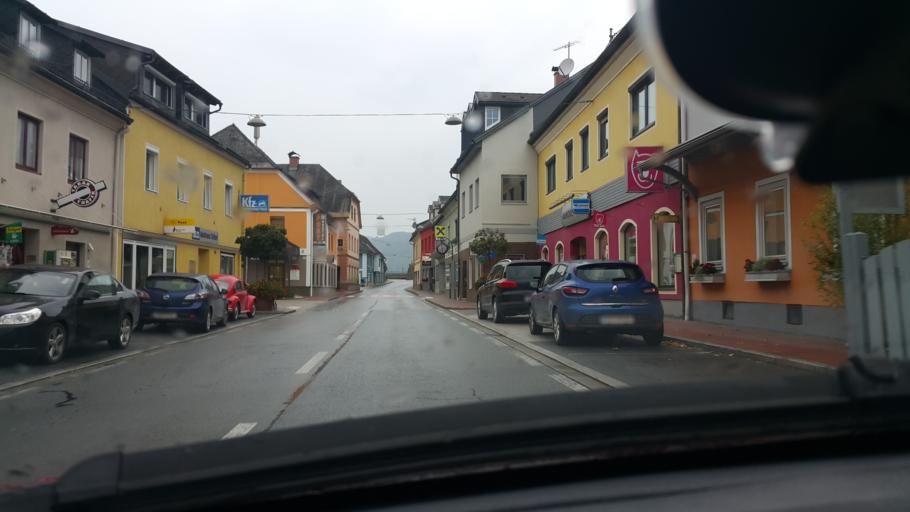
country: AT
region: Carinthia
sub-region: Politischer Bezirk Wolfsberg
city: Lavamund
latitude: 46.6420
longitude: 14.9412
